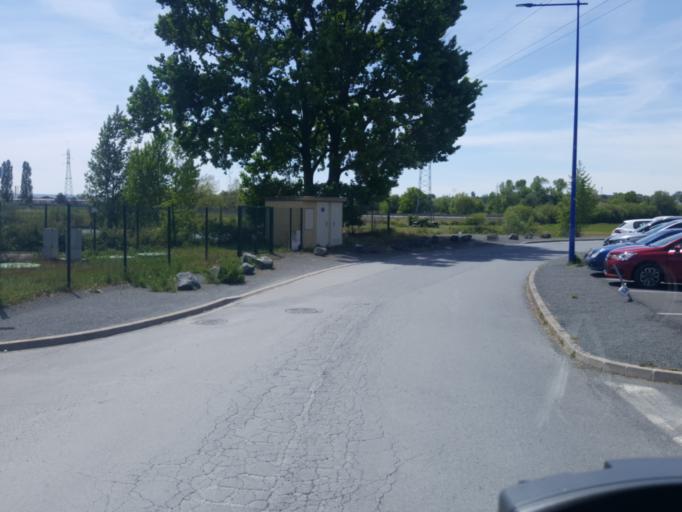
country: FR
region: Auvergne
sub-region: Departement de l'Allier
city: Saint-Victor
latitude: 46.3782
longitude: 2.5884
